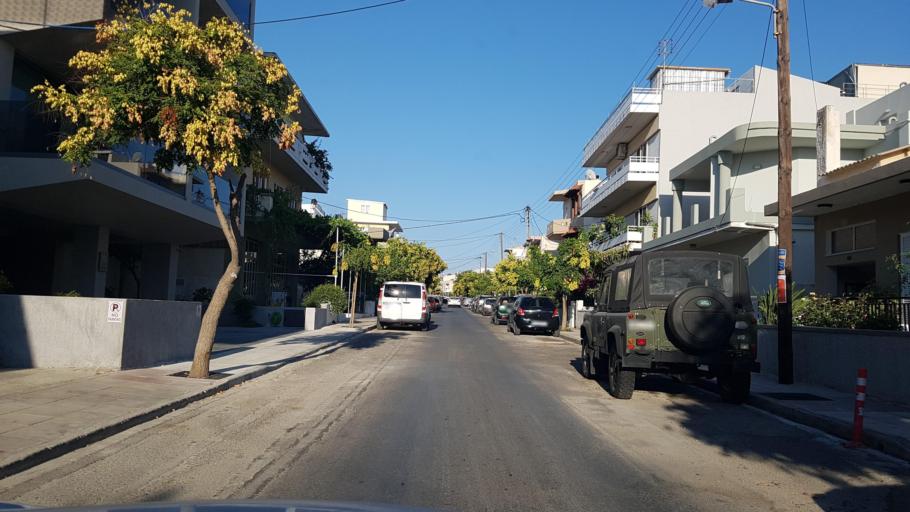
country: GR
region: Crete
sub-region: Nomos Chanias
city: Chania
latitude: 35.5074
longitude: 24.0107
